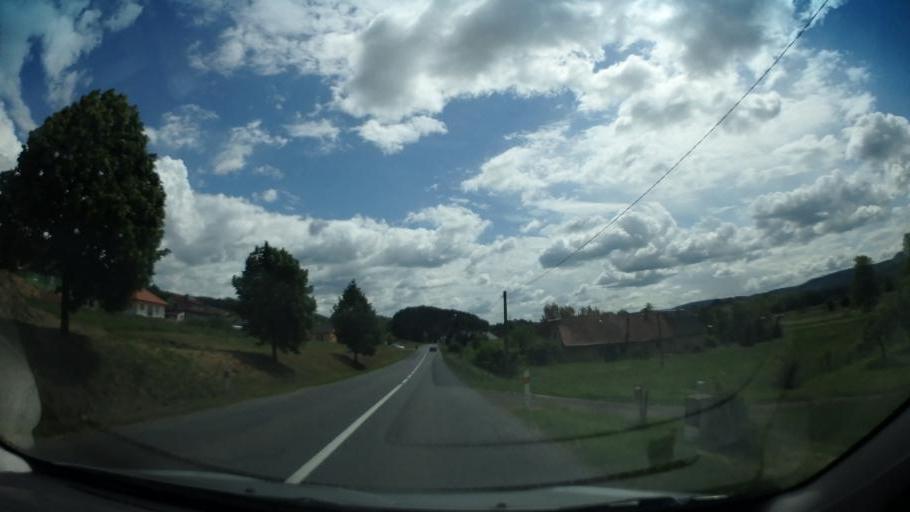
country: CZ
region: Pardubicky
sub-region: Okres Svitavy
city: Moravska Trebova
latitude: 49.7353
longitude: 16.6440
